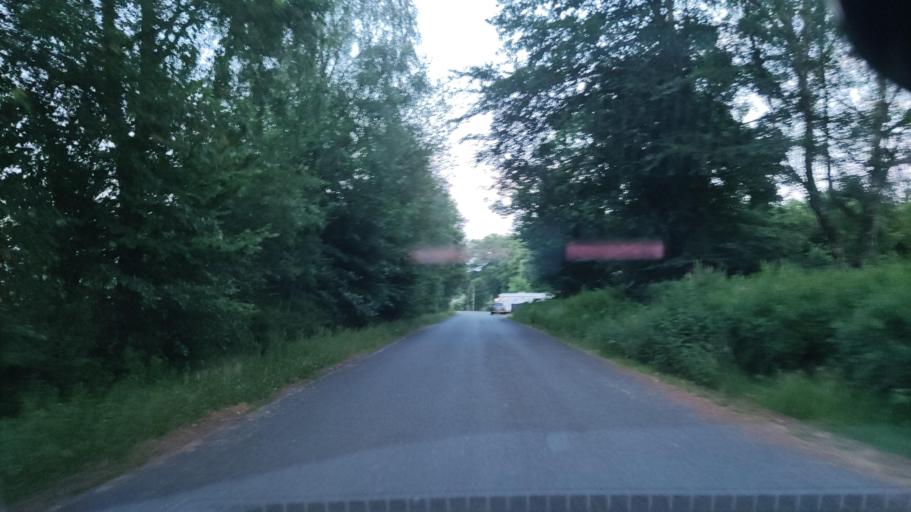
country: DE
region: Lower Saxony
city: Soderstorf
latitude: 53.1269
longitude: 10.1187
